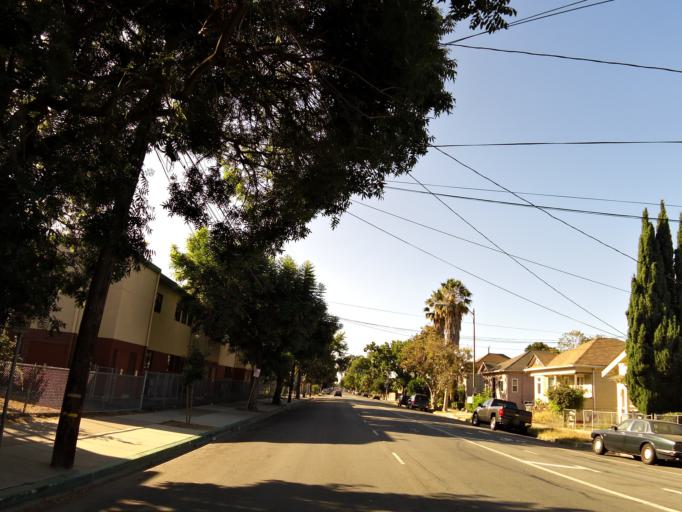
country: US
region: California
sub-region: Santa Clara County
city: San Jose
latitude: 37.3511
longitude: -121.8874
